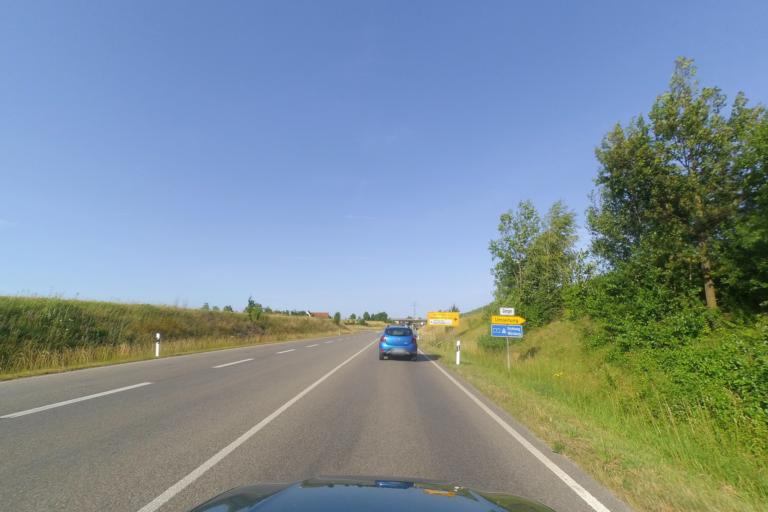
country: DE
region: Bavaria
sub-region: Swabia
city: Lauingen
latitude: 48.5755
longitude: 10.4094
